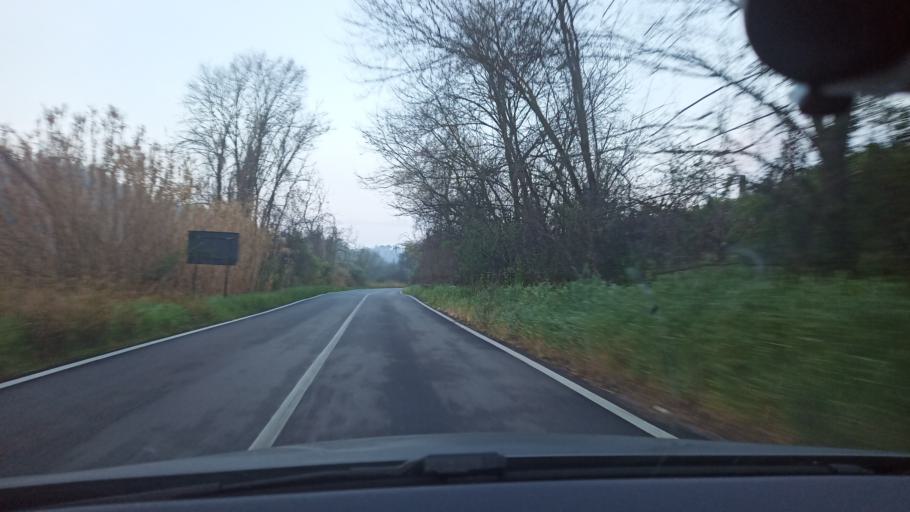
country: IT
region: Latium
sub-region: Provincia di Rieti
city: Cantalupo in Sabina
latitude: 42.2796
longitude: 12.6487
